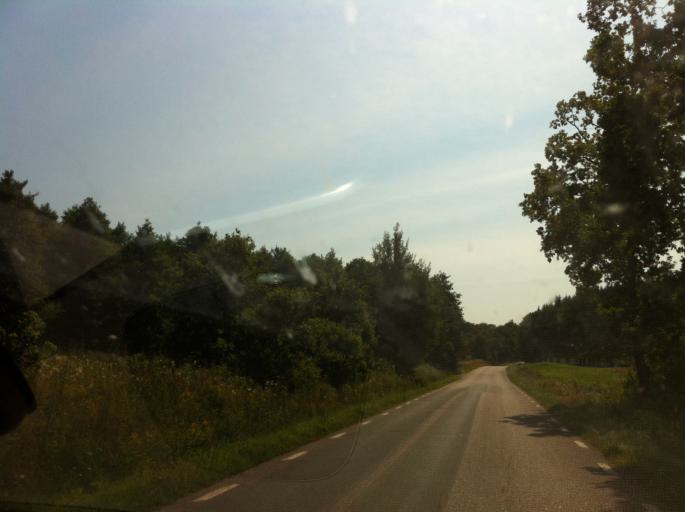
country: SE
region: Skane
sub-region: Hoors Kommun
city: Hoeoer
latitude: 56.0053
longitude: 13.4900
